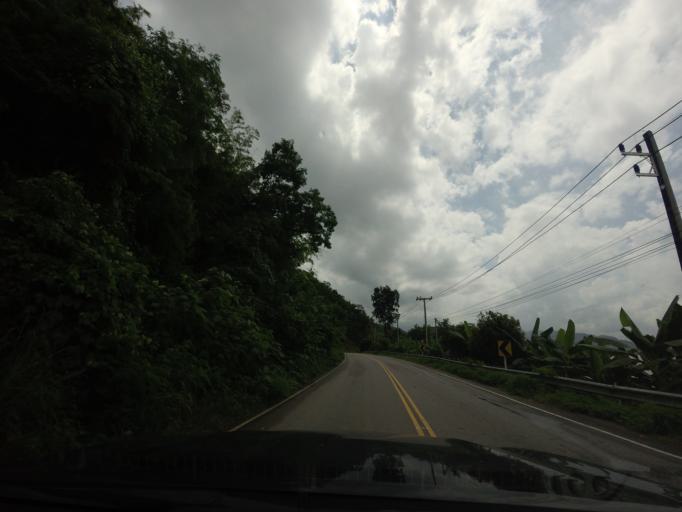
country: TH
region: Loei
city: Pak Chom
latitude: 18.0511
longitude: 101.7754
